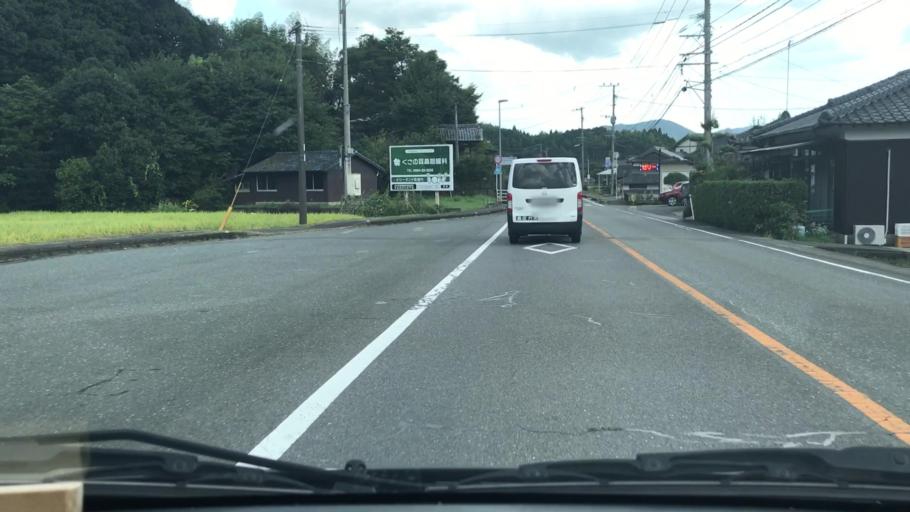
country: JP
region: Saga Prefecture
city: Takeocho-takeo
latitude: 33.2278
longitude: 130.0225
